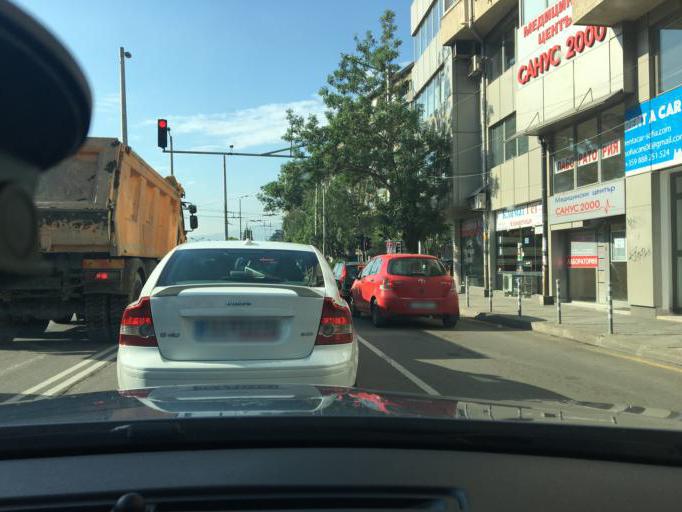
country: BG
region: Sofia-Capital
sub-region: Stolichna Obshtina
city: Sofia
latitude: 42.6848
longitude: 23.3008
